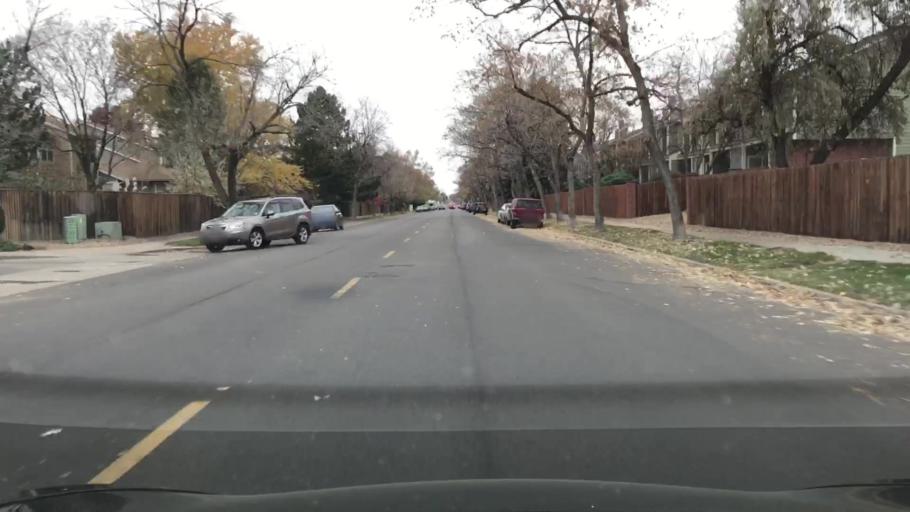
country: US
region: Colorado
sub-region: Arapahoe County
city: Glendale
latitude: 39.6894
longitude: -104.8986
